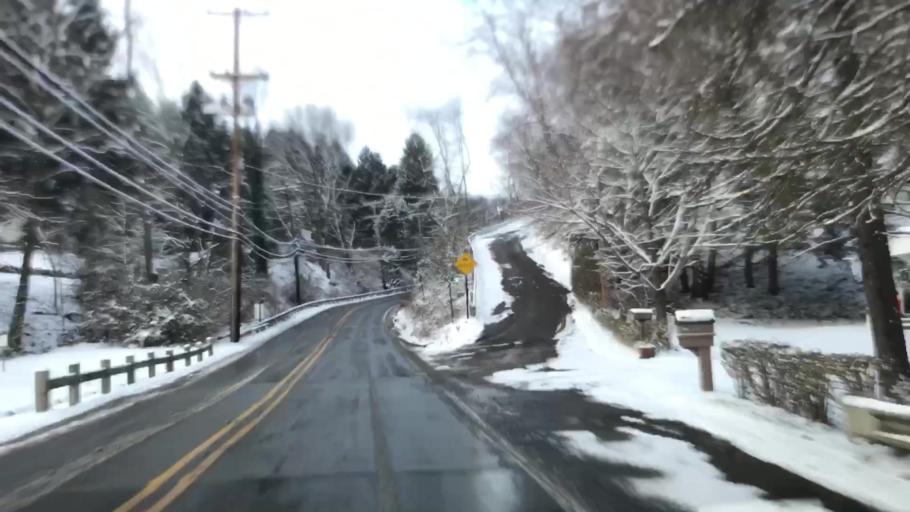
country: US
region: Pennsylvania
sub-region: Allegheny County
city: West View
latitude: 40.5387
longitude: -80.0513
